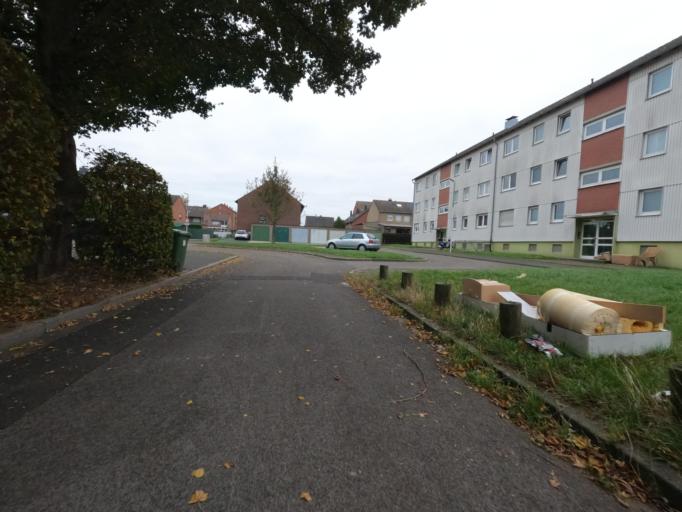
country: DE
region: North Rhine-Westphalia
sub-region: Regierungsbezirk Koln
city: Linnich
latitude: 50.9723
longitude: 6.2660
